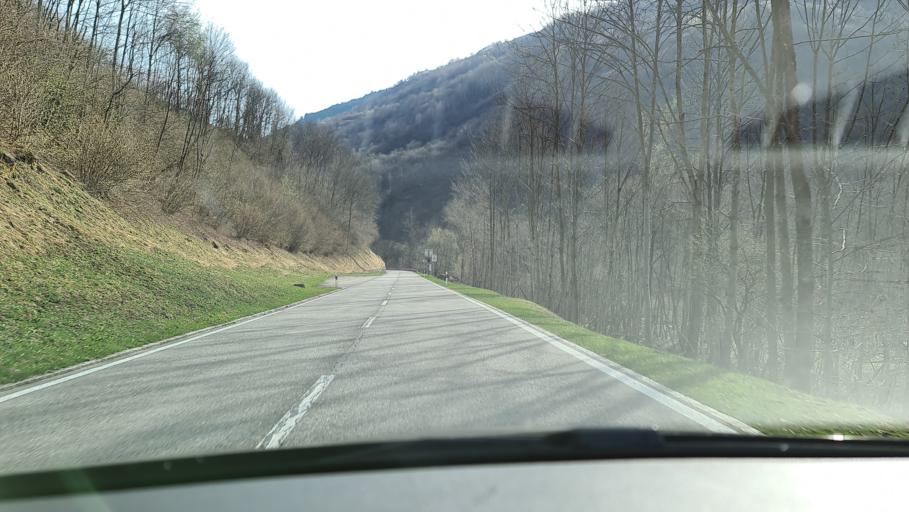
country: CH
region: Ticino
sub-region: Blenio District
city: Acquarossa
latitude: 46.5222
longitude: 8.9392
